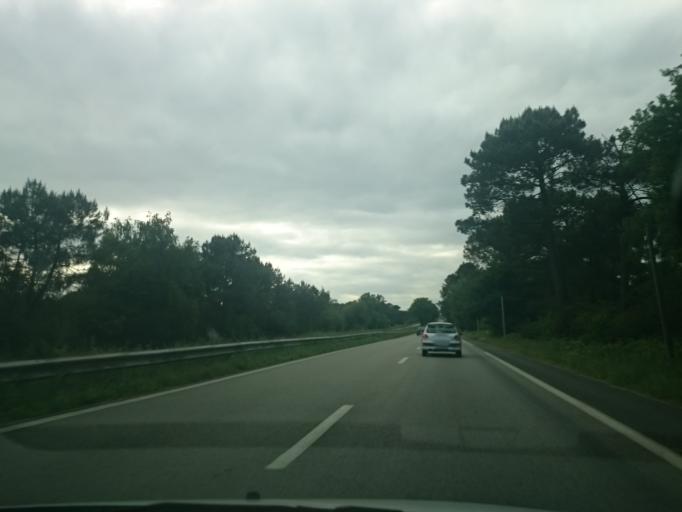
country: FR
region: Brittany
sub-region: Departement du Morbihan
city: Landaul
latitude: 47.7348
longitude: -3.0937
